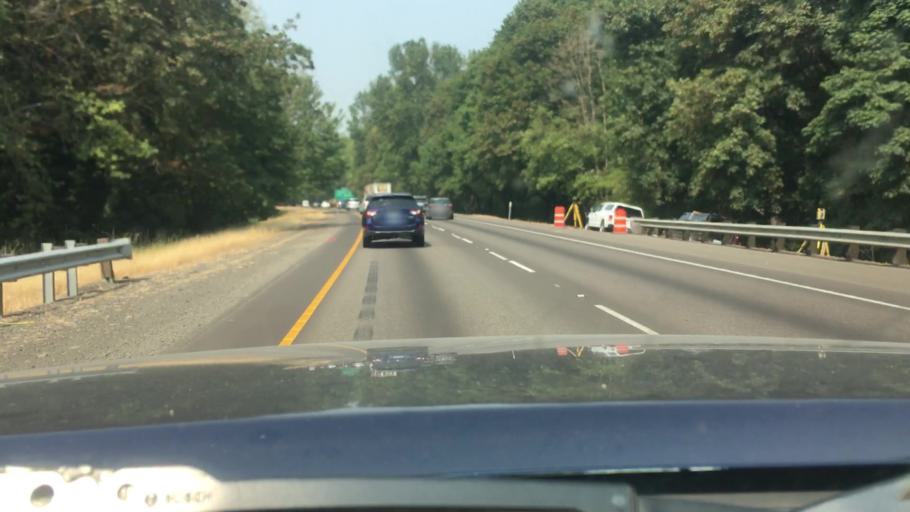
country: US
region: Oregon
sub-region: Clackamas County
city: Stafford
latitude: 45.3647
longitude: -122.6746
